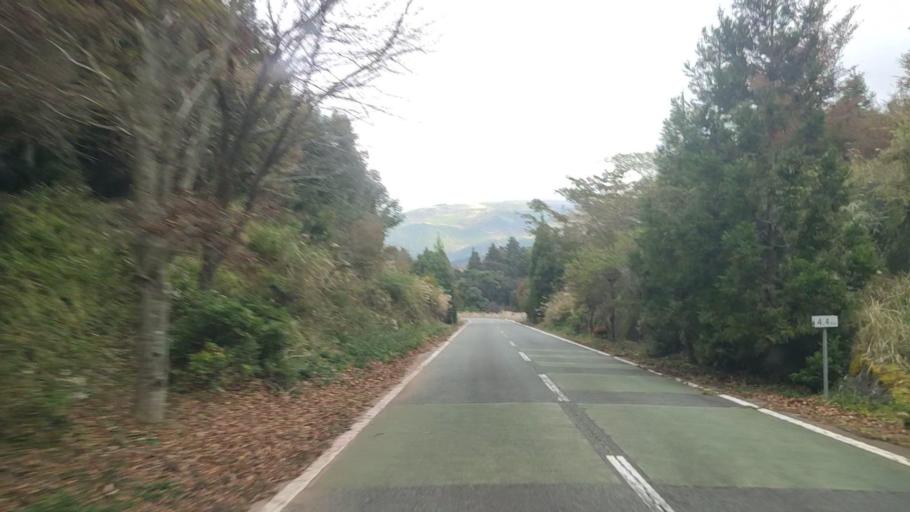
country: JP
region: Shizuoka
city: Heda
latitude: 34.8982
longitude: 138.8462
